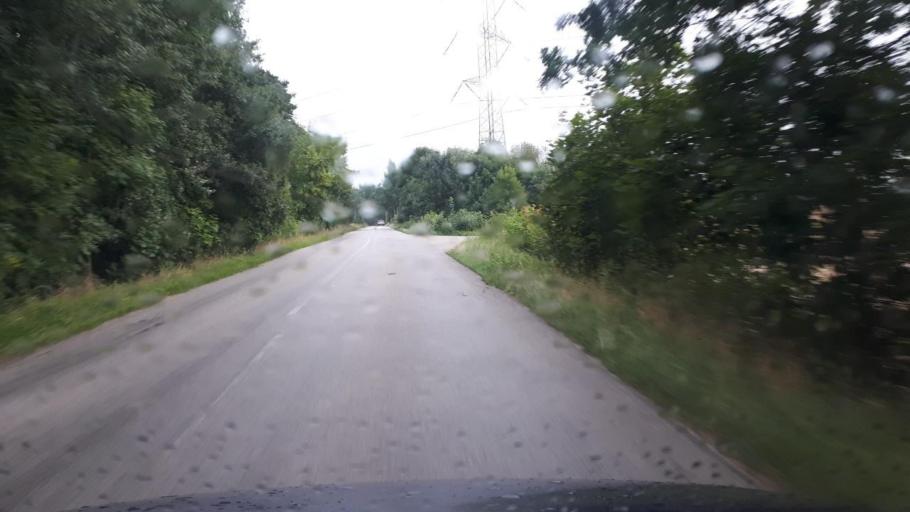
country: PL
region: Silesian Voivodeship
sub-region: Powiat tarnogorski
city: Wieszowa
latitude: 50.3781
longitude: 18.7154
